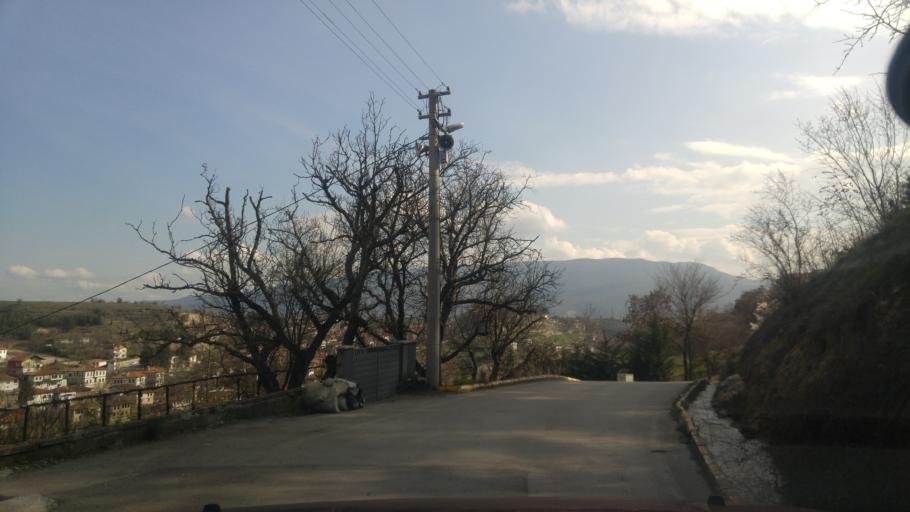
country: TR
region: Karabuk
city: Safranbolu
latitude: 41.2528
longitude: 32.6860
